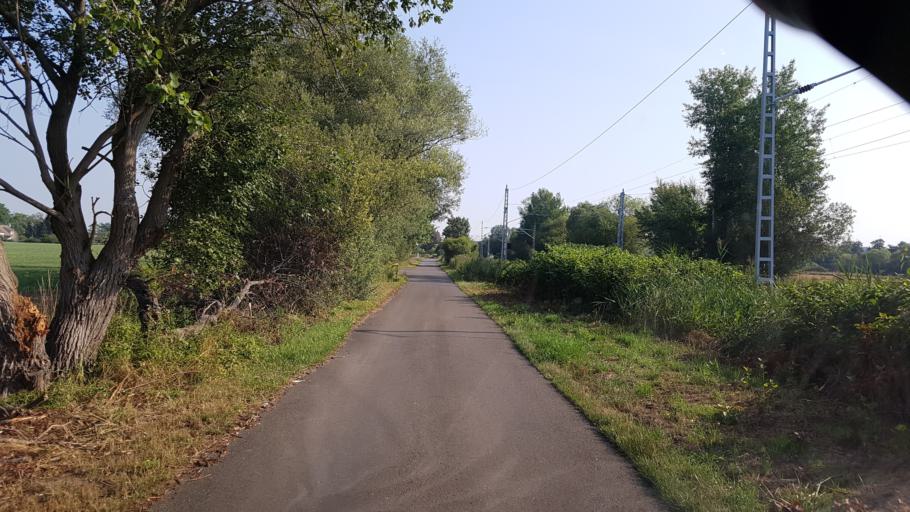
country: DE
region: Brandenburg
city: Drebkau
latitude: 51.6881
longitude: 14.2517
